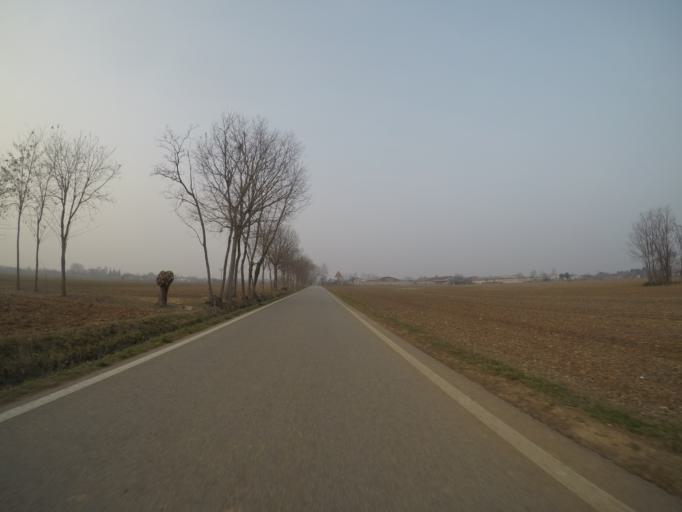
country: IT
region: Veneto
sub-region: Provincia di Treviso
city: Altivole
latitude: 45.7427
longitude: 11.9593
